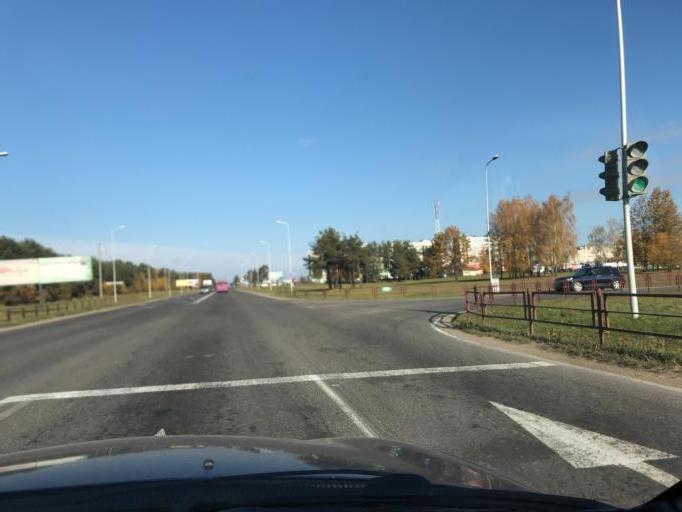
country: BY
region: Grodnenskaya
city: Lida
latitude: 53.8889
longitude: 25.2533
